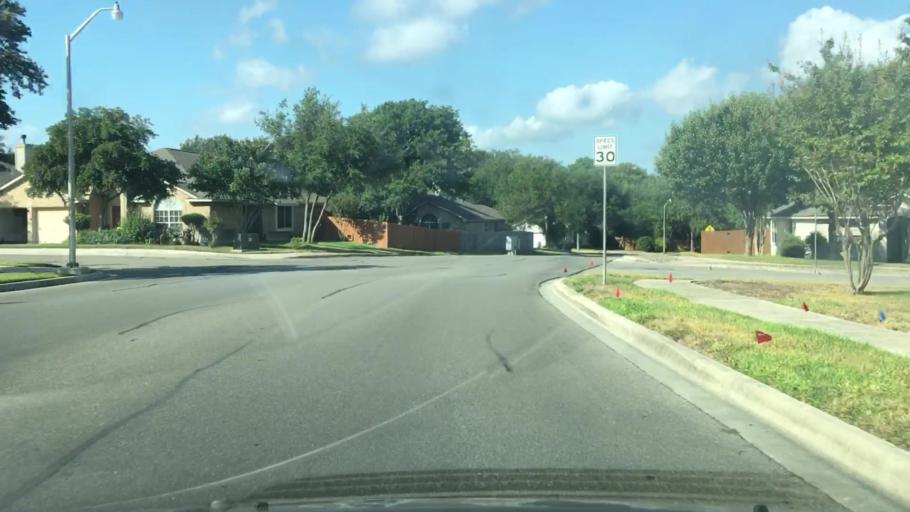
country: US
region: Texas
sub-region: Guadalupe County
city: Schertz
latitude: 29.5808
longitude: -98.2537
